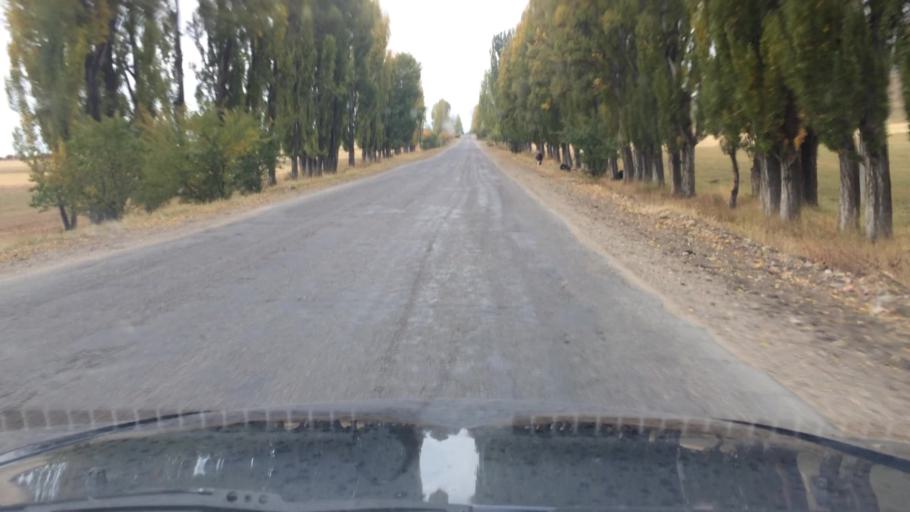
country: KG
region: Ysyk-Koel
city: Pokrovka
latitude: 42.7363
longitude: 77.9586
